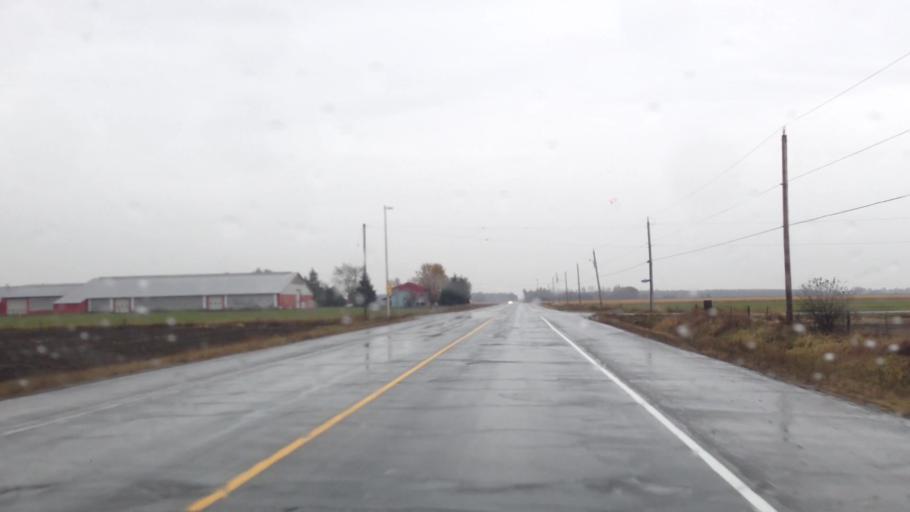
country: CA
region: Ontario
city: Clarence-Rockland
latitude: 45.4523
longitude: -75.4251
